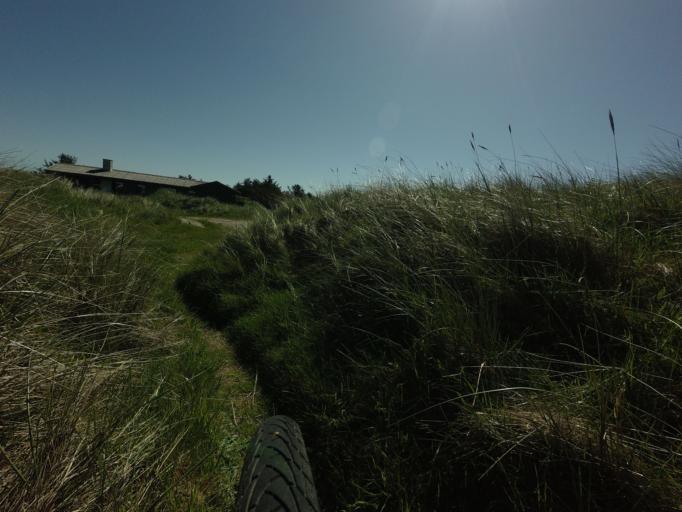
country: DK
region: North Denmark
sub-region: Jammerbugt Kommune
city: Pandrup
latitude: 57.3123
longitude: 9.6541
